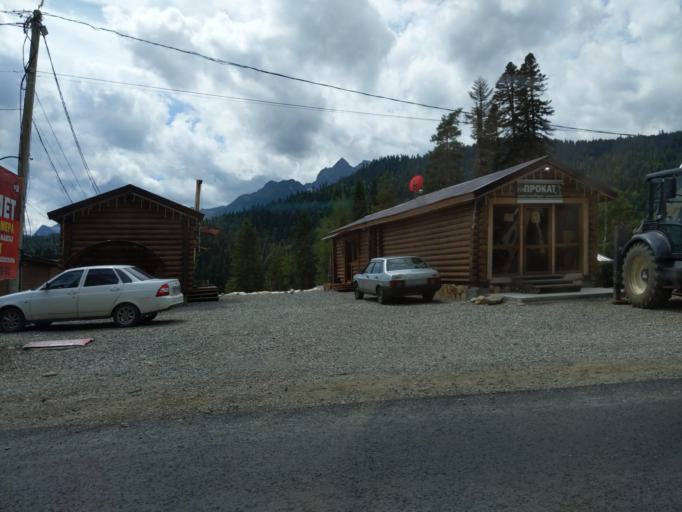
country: RU
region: Karachayevo-Cherkesiya
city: Nizhniy Arkhyz
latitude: 43.5372
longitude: 41.2098
